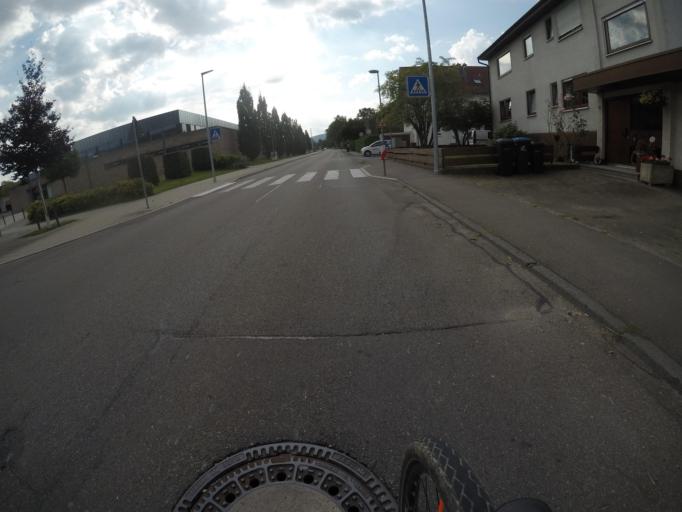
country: DE
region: Baden-Wuerttemberg
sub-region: Tuebingen Region
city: Dettingen an der Erms
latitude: 48.5260
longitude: 9.3537
